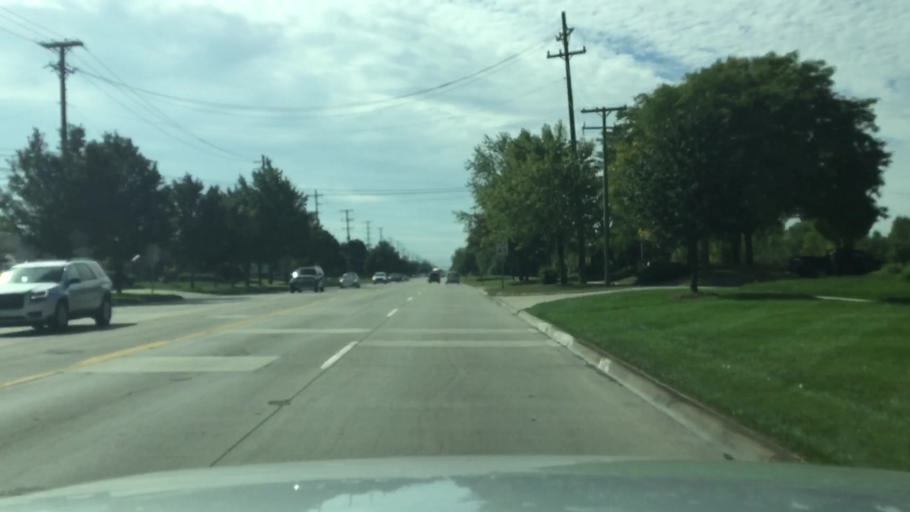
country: US
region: Michigan
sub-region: Wayne County
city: Canton
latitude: 42.3276
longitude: -83.4883
